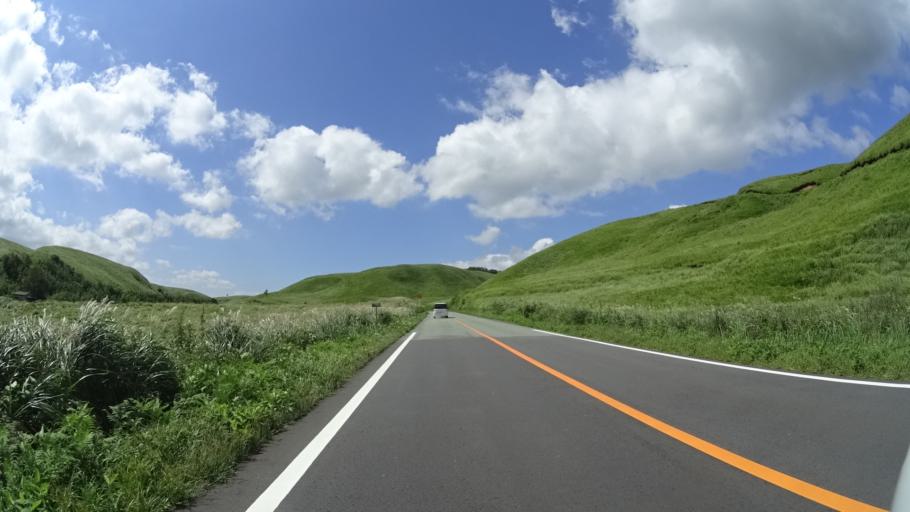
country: JP
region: Kumamoto
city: Aso
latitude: 33.0111
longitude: 131.1497
